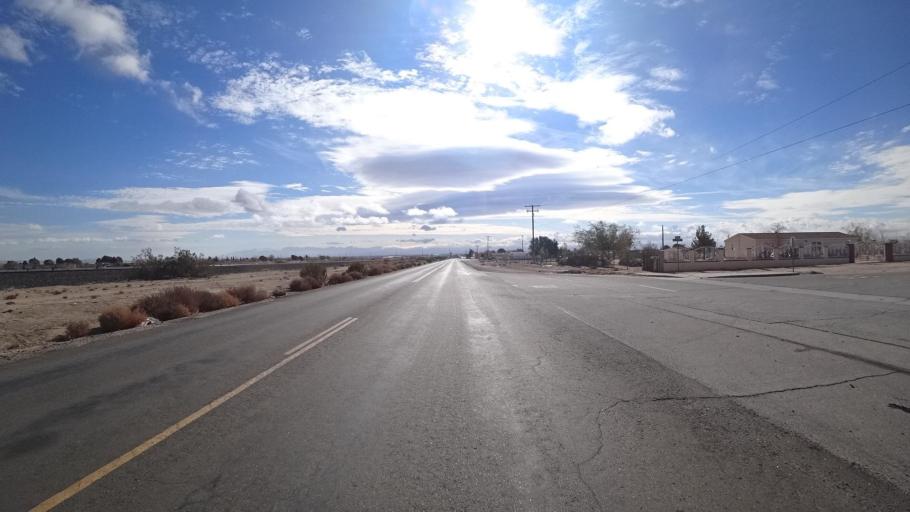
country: US
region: California
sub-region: Kern County
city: Rosamond
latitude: 34.8719
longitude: -118.1643
